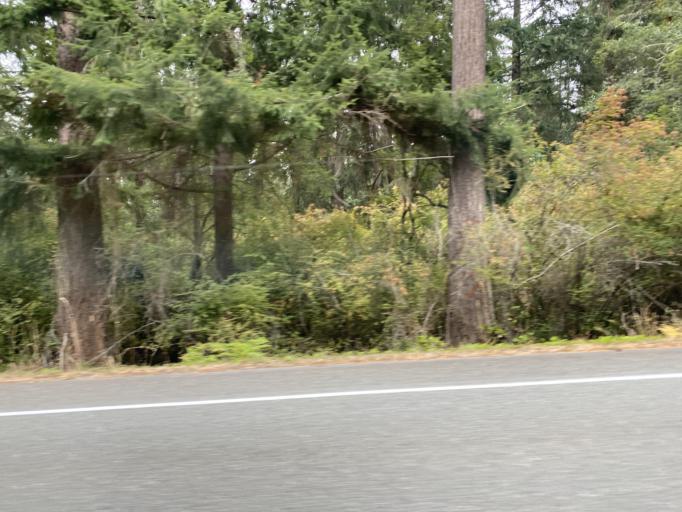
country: US
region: Washington
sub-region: Island County
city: Coupeville
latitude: 48.2163
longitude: -122.6375
